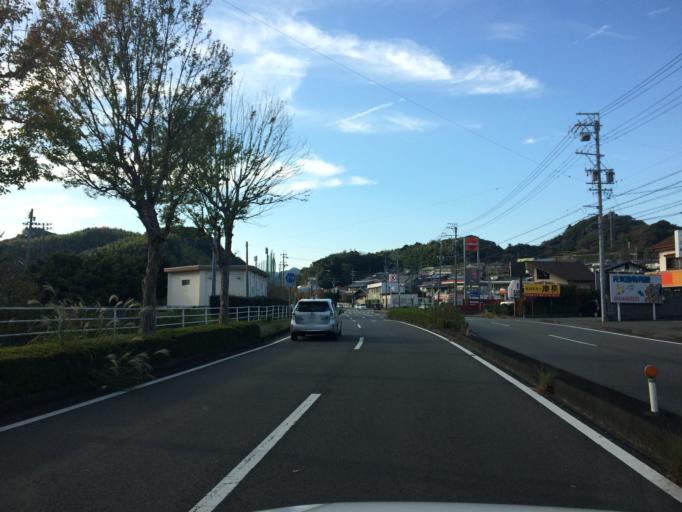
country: JP
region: Shizuoka
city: Fujieda
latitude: 34.8657
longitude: 138.2379
